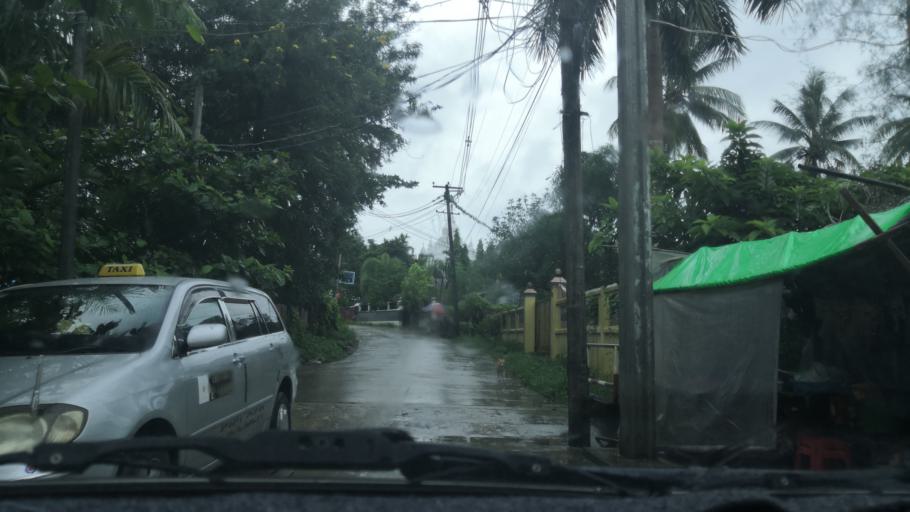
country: MM
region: Yangon
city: Yangon
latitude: 16.8827
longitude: 96.1490
